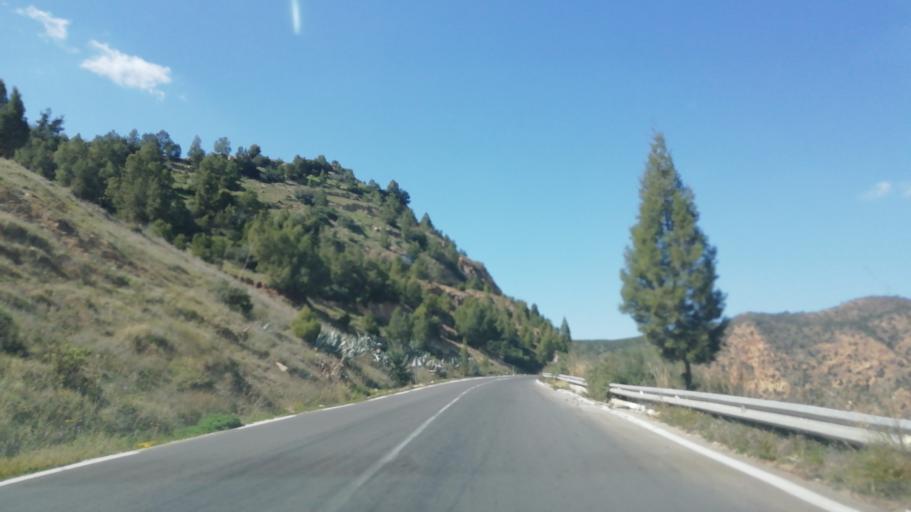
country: DZ
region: Mascara
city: Mascara
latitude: 35.4979
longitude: 0.1345
